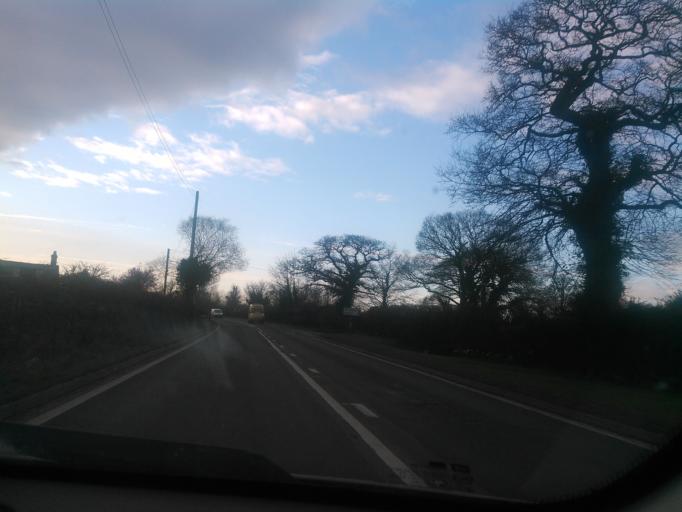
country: GB
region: England
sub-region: Shropshire
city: Stoke upon Tern
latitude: 52.8663
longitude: -2.5006
